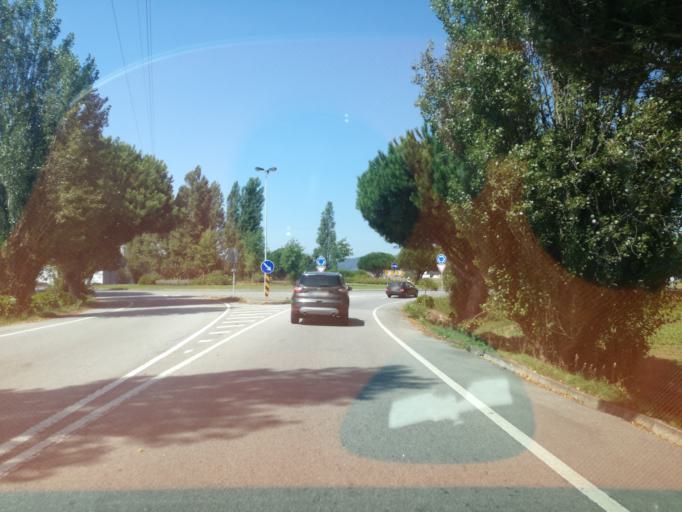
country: PT
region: Braga
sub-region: Esposende
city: Esposende
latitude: 41.5243
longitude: -8.7724
